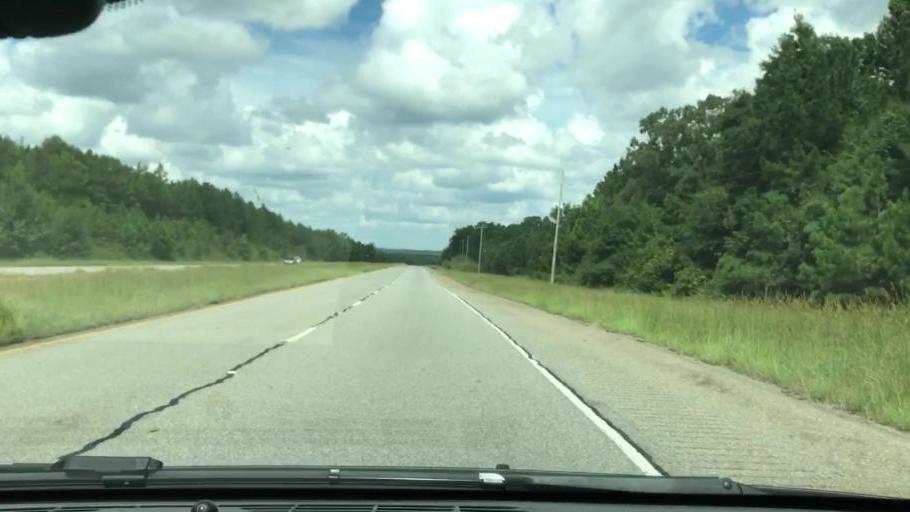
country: US
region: Georgia
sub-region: Stewart County
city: Lumpkin
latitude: 32.1186
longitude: -84.8153
